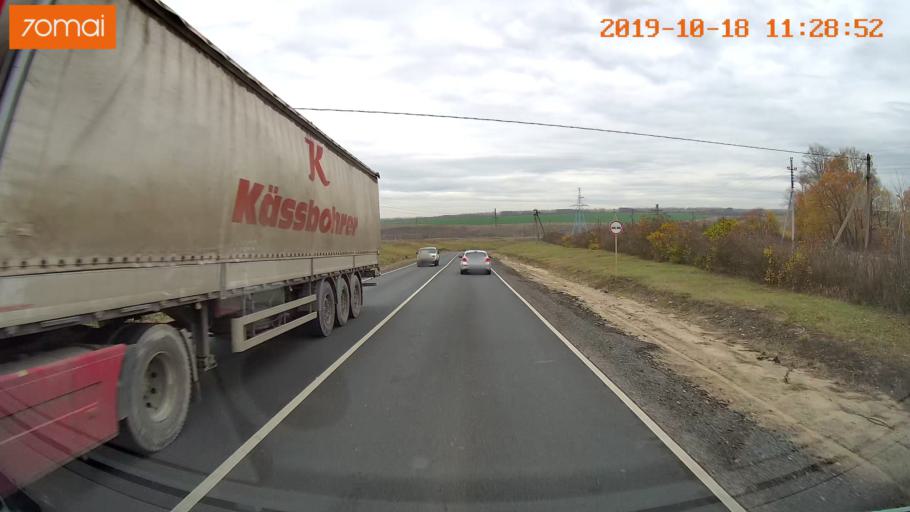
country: RU
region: Tula
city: Kimovsk
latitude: 54.1568
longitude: 38.6679
